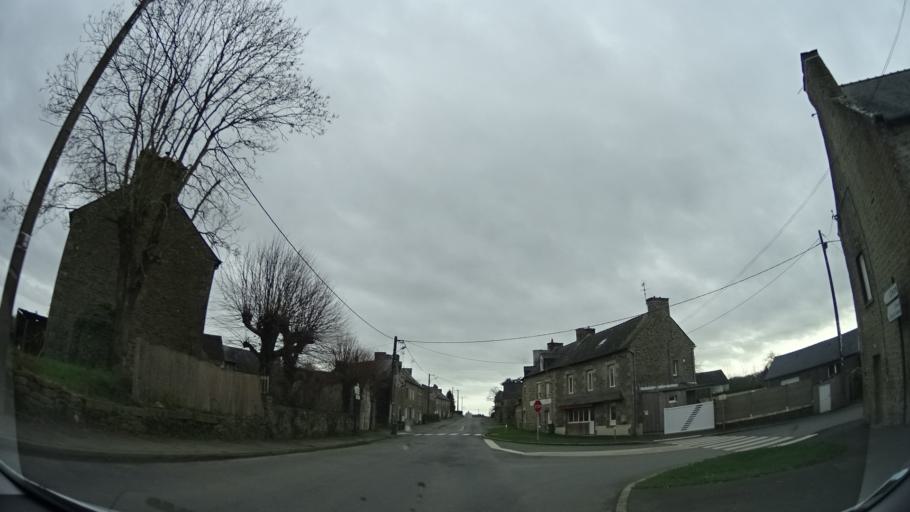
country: FR
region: Brittany
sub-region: Departement des Cotes-d'Armor
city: Dinan
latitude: 48.4370
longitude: -2.0146
